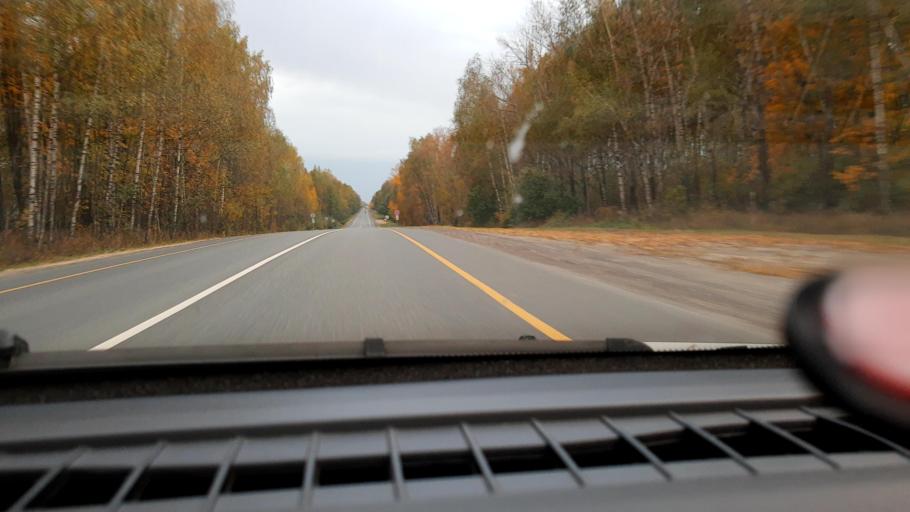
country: RU
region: Vladimir
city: Orgtrud
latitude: 56.2011
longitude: 40.7957
